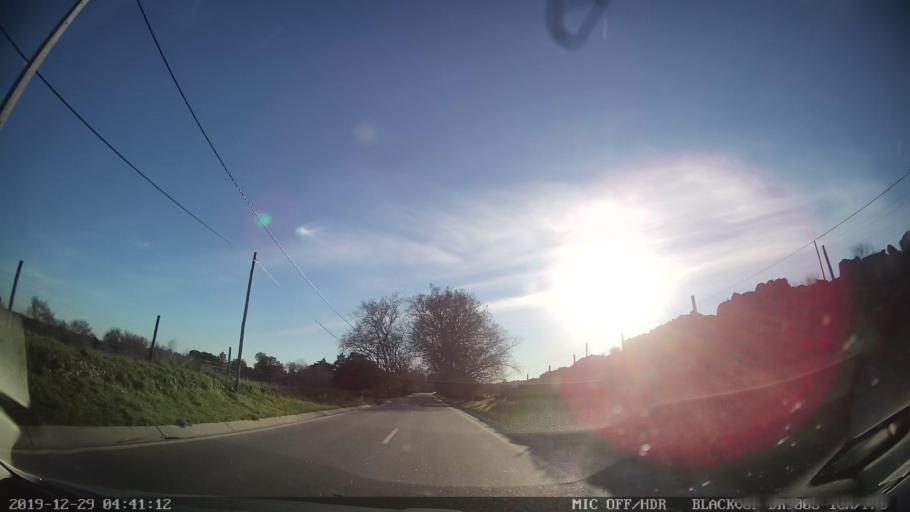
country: PT
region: Guarda
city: Alcains
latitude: 39.9169
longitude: -7.4125
